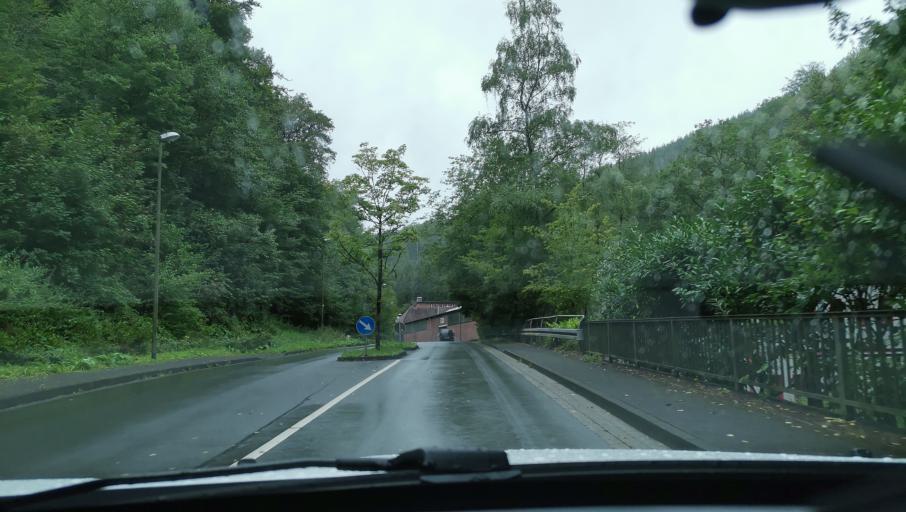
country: DE
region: North Rhine-Westphalia
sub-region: Regierungsbezirk Arnsberg
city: Schalksmuhle
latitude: 51.2516
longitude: 7.5097
